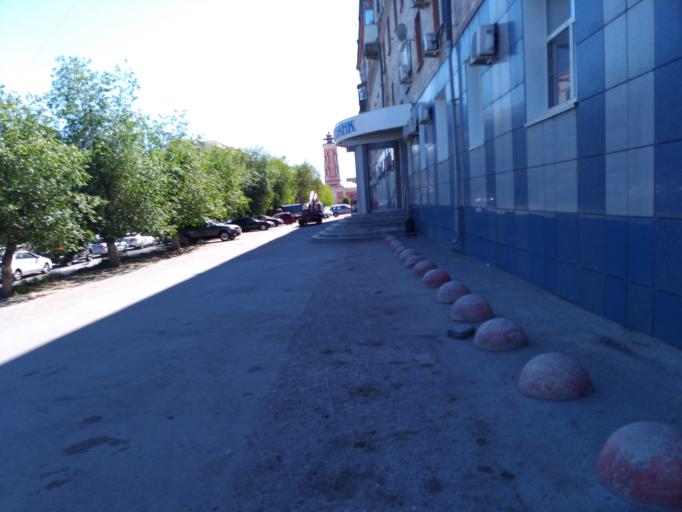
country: RU
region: Volgograd
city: Volgograd
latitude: 48.7113
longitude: 44.5131
